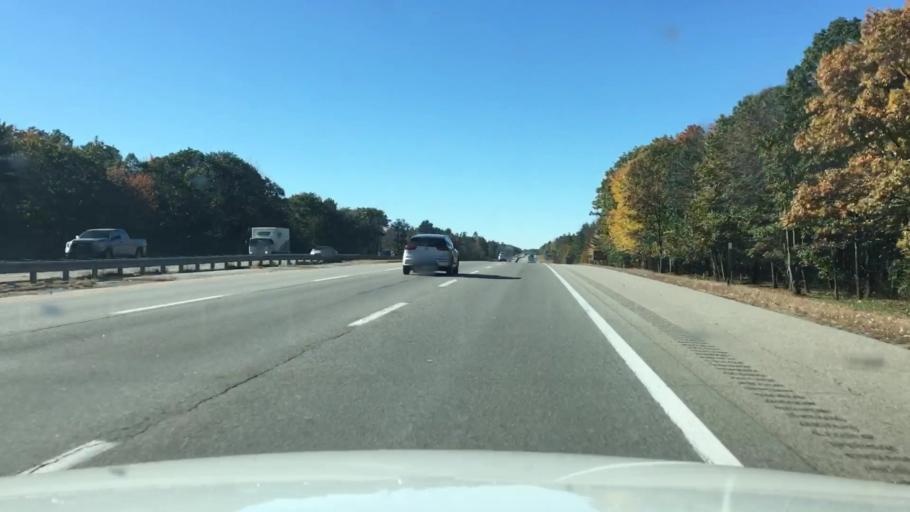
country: US
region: Maine
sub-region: Cumberland County
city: West Scarborough
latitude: 43.5534
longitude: -70.4261
